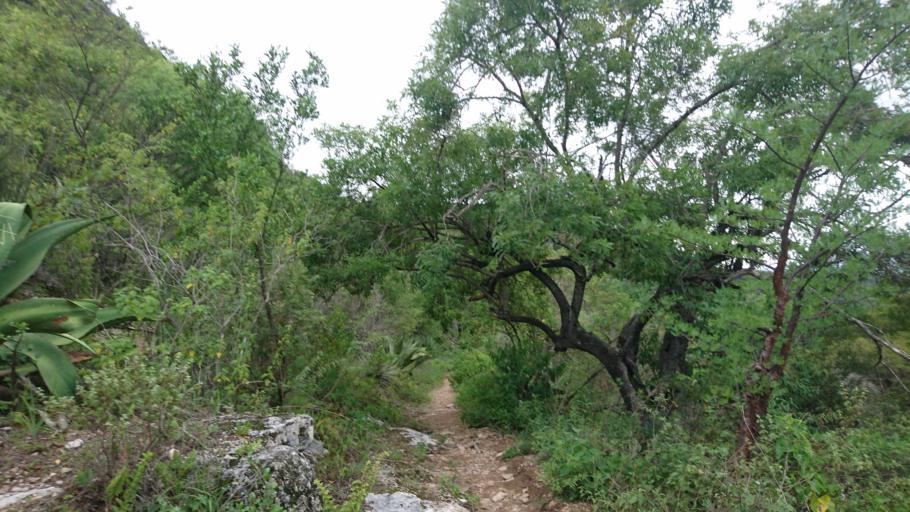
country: MX
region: Oaxaca
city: San Lorenzo Albarradas
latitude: 16.8649
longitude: -96.2751
